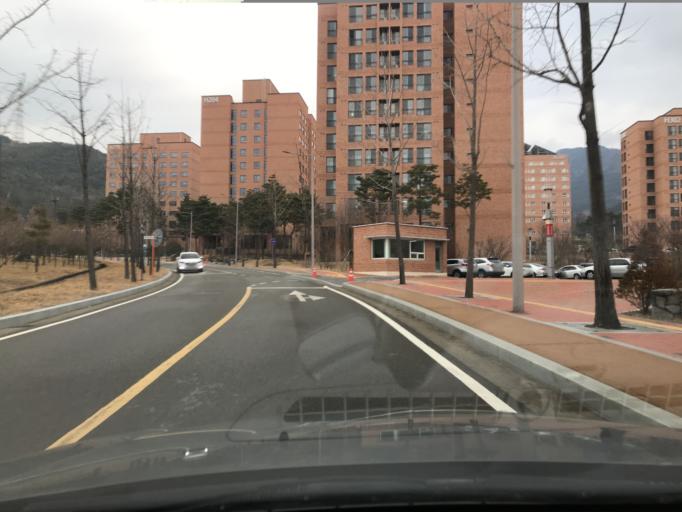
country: KR
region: Daegu
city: Hwawon
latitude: 35.7021
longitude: 128.4608
